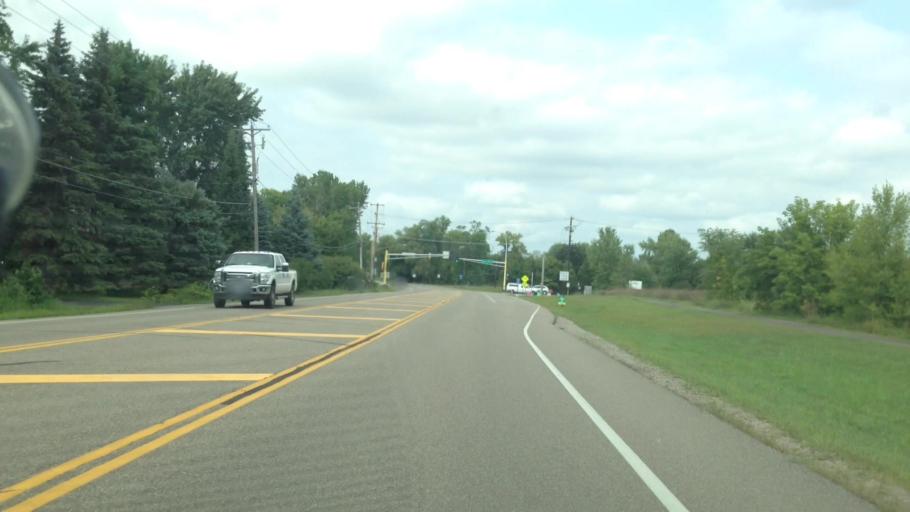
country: US
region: Minnesota
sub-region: Anoka County
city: Circle Pines
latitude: 45.1407
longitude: -93.1265
